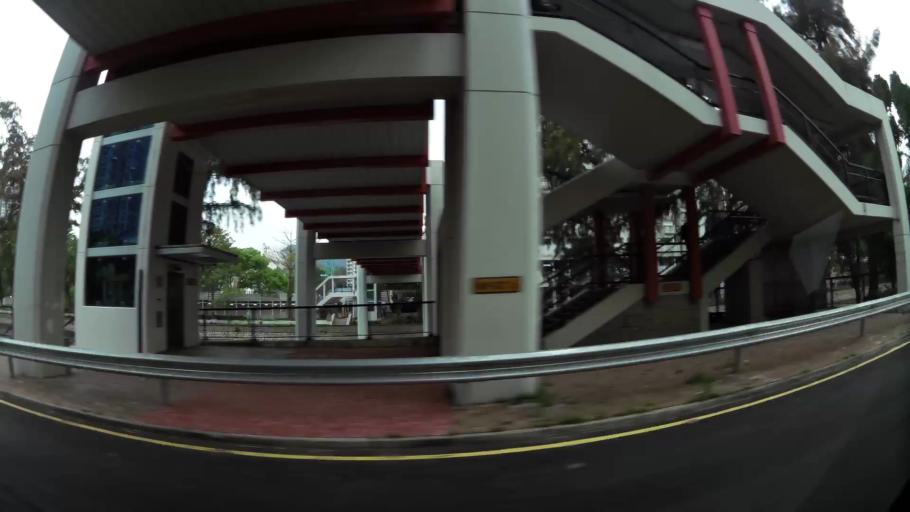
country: HK
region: Tai Po
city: Tai Po
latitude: 22.4510
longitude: 114.1694
